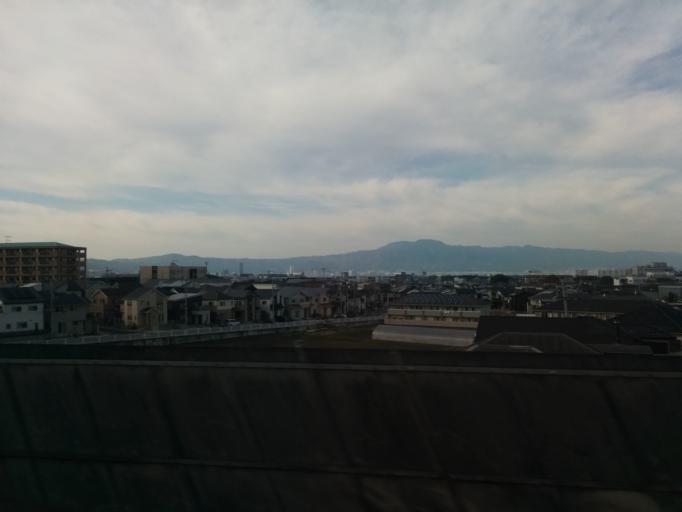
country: JP
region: Shiga Prefecture
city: Kusatsu
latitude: 34.9843
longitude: 135.9443
